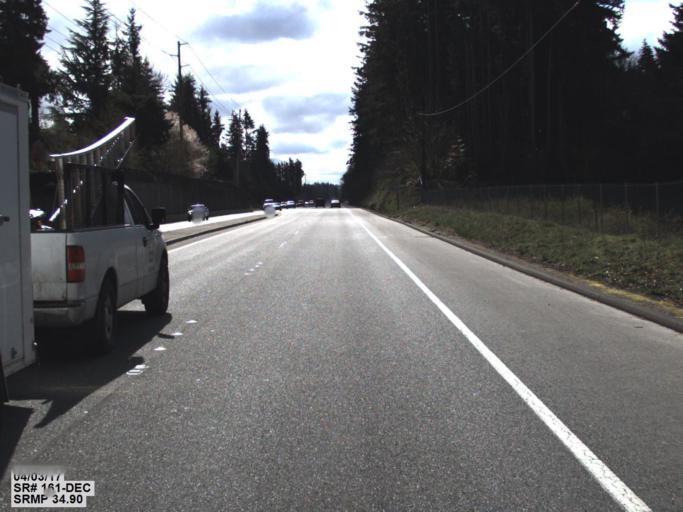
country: US
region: Washington
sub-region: King County
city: Lakeland South
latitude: 47.2712
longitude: -122.3049
